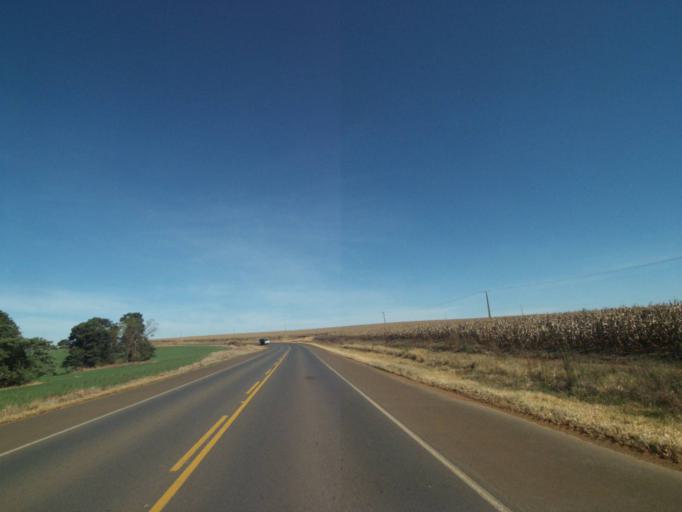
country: BR
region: Parana
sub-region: Tibagi
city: Tibagi
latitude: -24.3902
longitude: -50.3357
